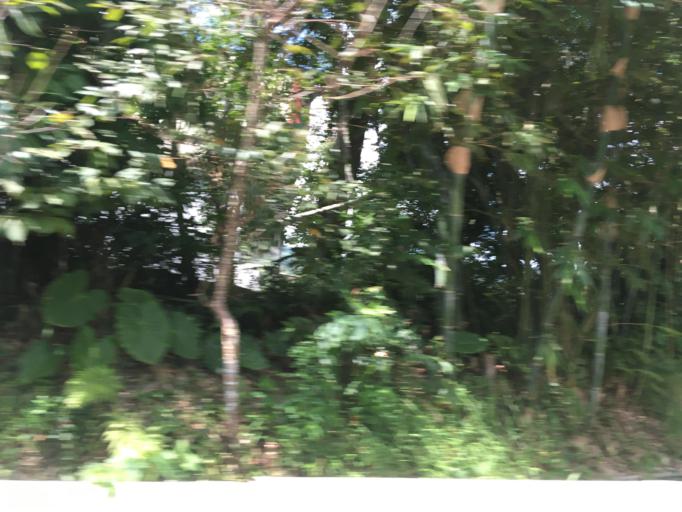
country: TW
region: Taiwan
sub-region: Yilan
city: Yilan
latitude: 24.9328
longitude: 121.6918
